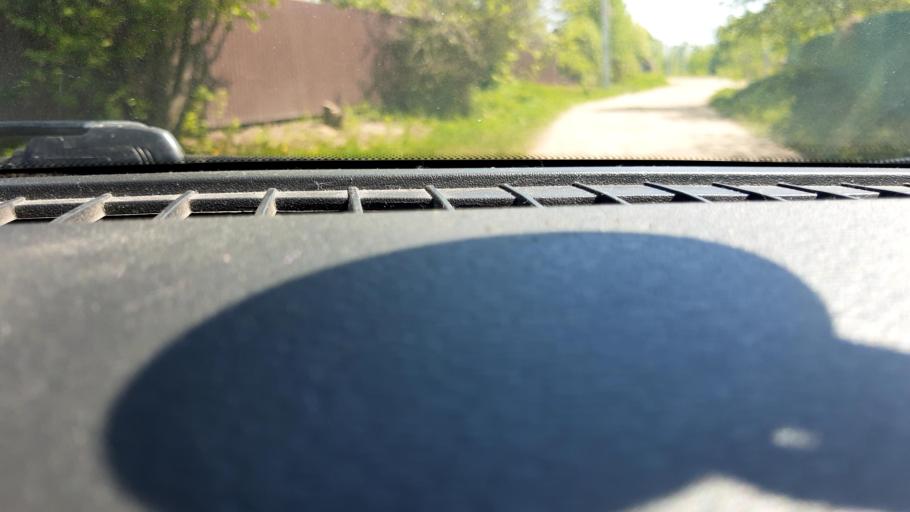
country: RU
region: Bashkortostan
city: Iglino
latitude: 54.7711
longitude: 56.1951
